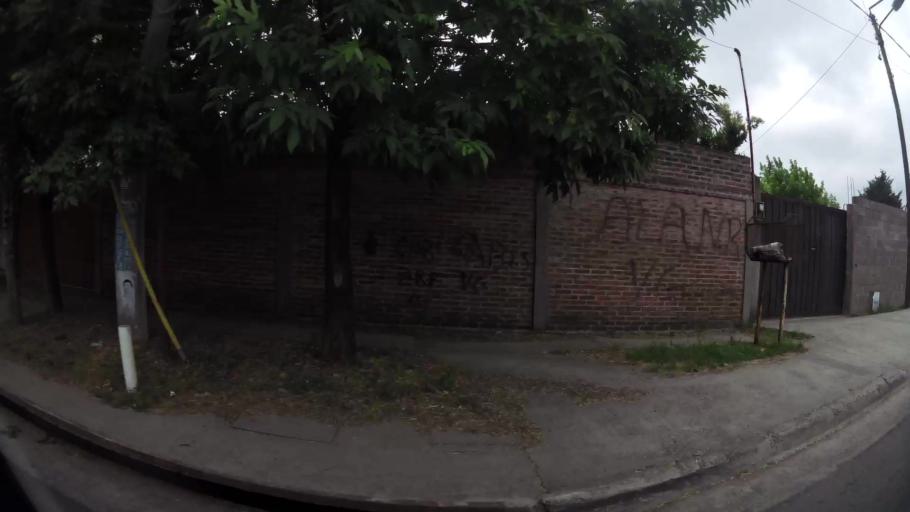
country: AR
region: Buenos Aires
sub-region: Partido de Ezeiza
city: Ezeiza
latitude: -34.8444
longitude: -58.5129
